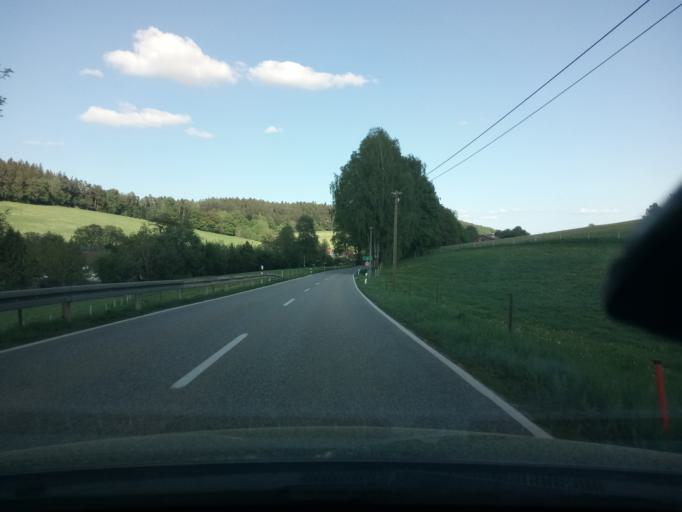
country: DE
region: Bavaria
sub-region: Upper Bavaria
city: Aschau am Inn
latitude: 48.2038
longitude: 12.3247
